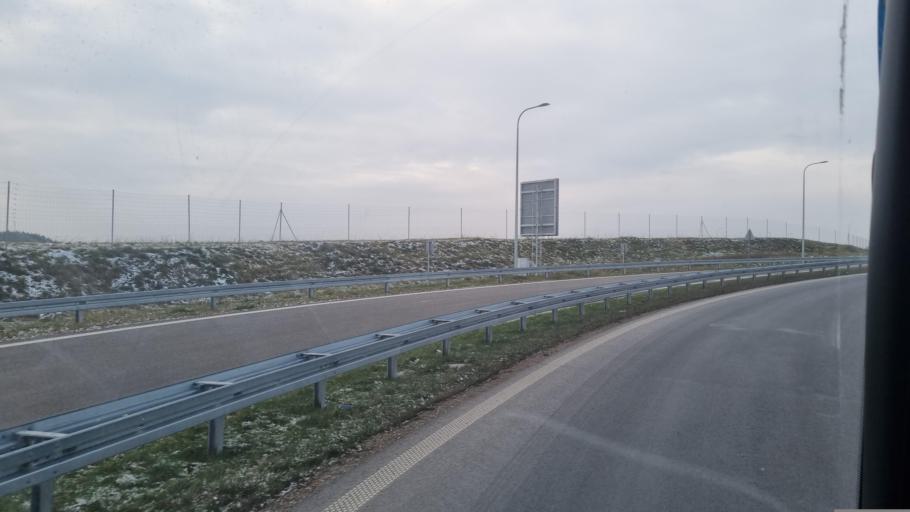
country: PL
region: Podlasie
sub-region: Powiat grajewski
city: Rajgrod
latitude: 53.8549
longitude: 22.5843
